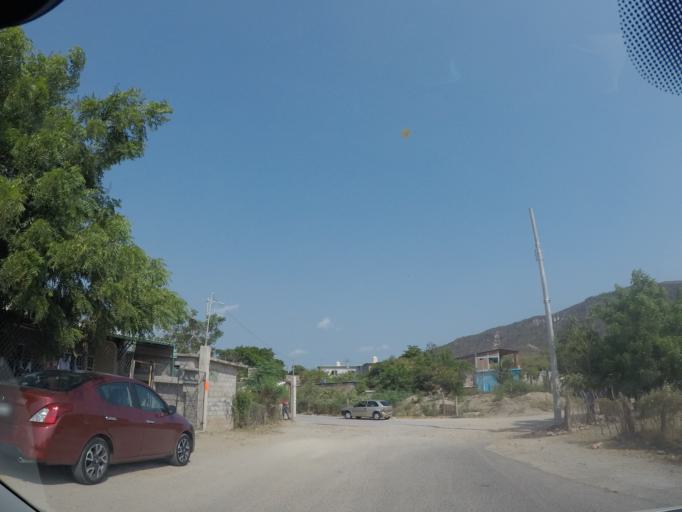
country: MX
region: Oaxaca
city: San Jeronimo Ixtepec
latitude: 16.5408
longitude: -95.0866
